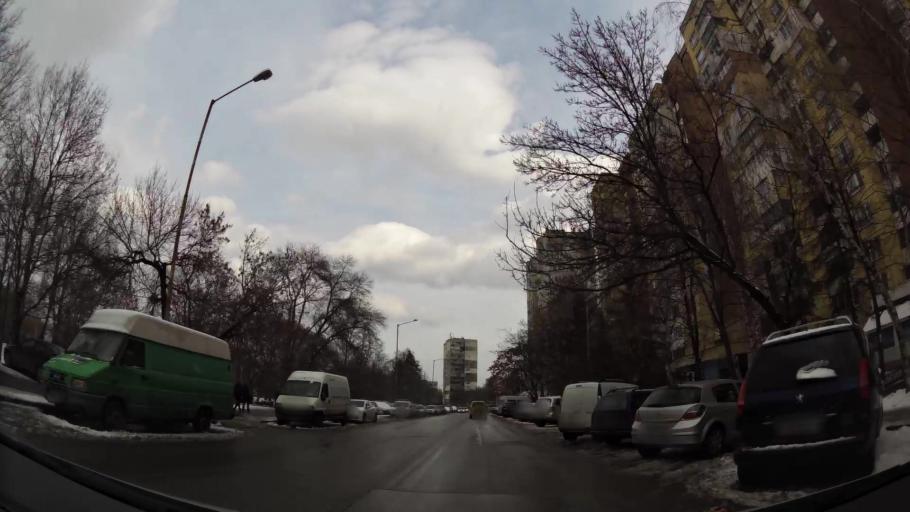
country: BG
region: Sofia-Capital
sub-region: Stolichna Obshtina
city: Sofia
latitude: 42.7027
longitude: 23.3620
